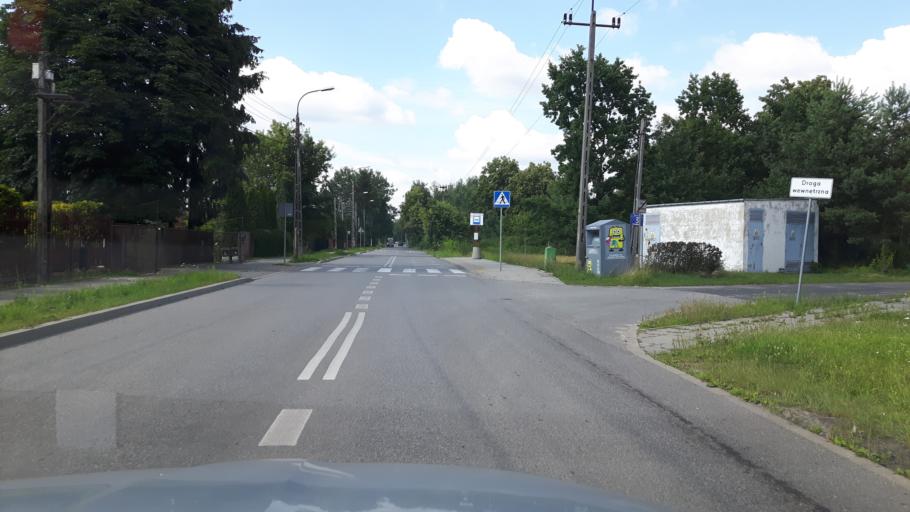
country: PL
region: Masovian Voivodeship
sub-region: Warszawa
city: Rembertow
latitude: 52.2813
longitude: 21.1717
